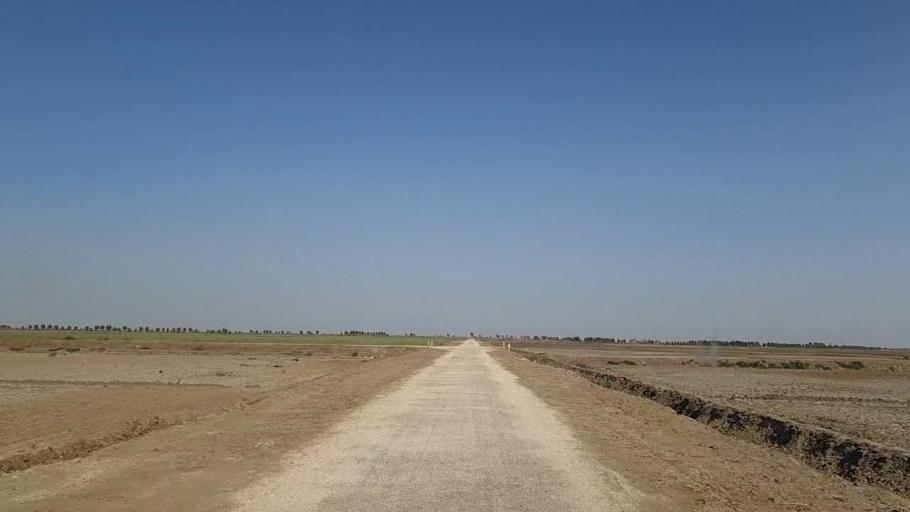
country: PK
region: Sindh
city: Jati
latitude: 24.5132
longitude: 68.1983
